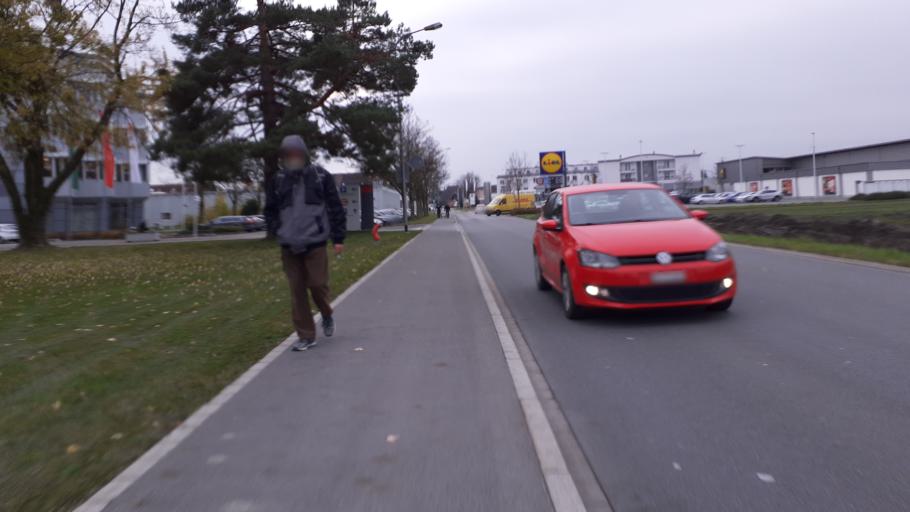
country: CH
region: Saint Gallen
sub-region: Wahlkreis Rheintal
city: Au
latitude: 47.4175
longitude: 9.6355
